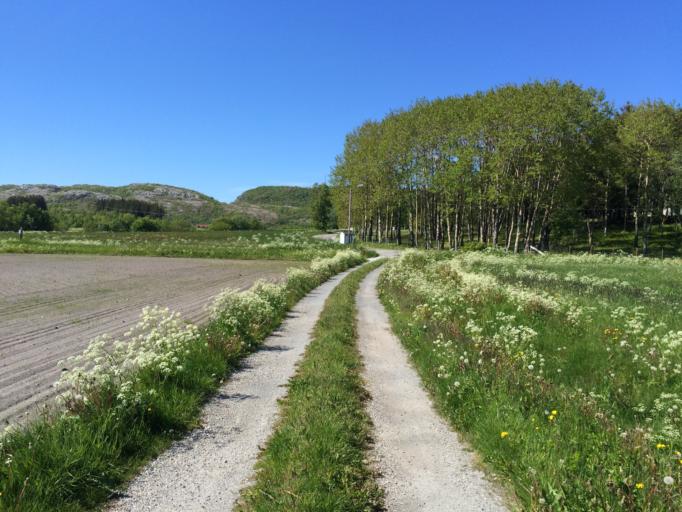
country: NO
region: Nordland
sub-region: Vevelstad
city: Vevelstad
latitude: 65.7724
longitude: 12.4562
